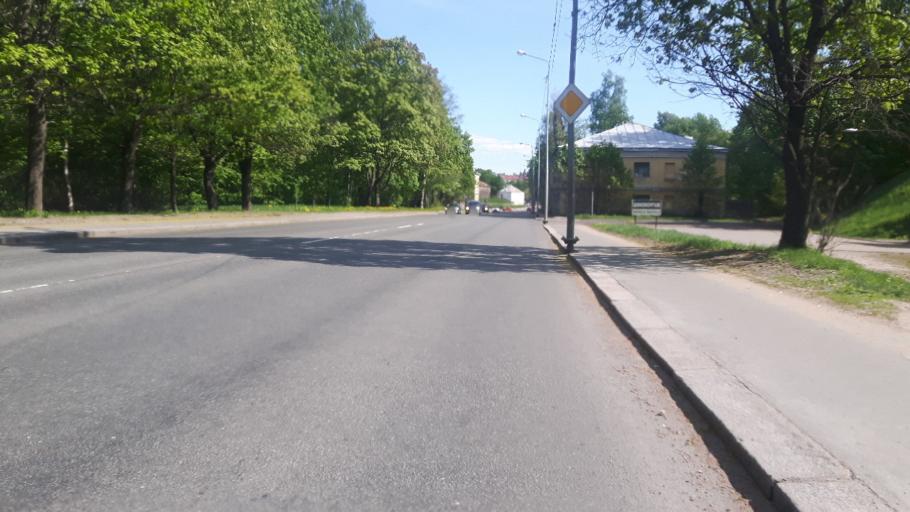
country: RU
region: Leningrad
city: Vyborg
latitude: 60.7188
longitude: 28.7210
